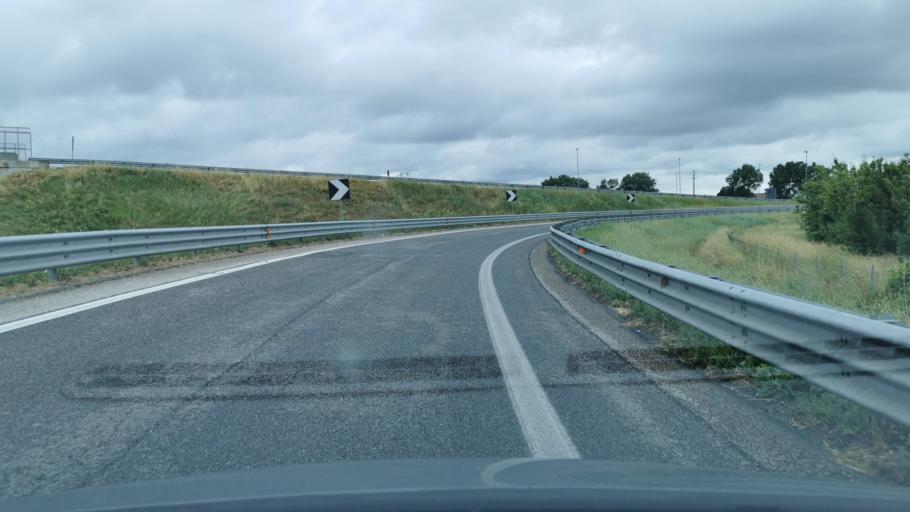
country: IT
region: Emilia-Romagna
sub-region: Provincia di Ravenna
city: Bagnacavallo
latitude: 44.4027
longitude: 11.9697
